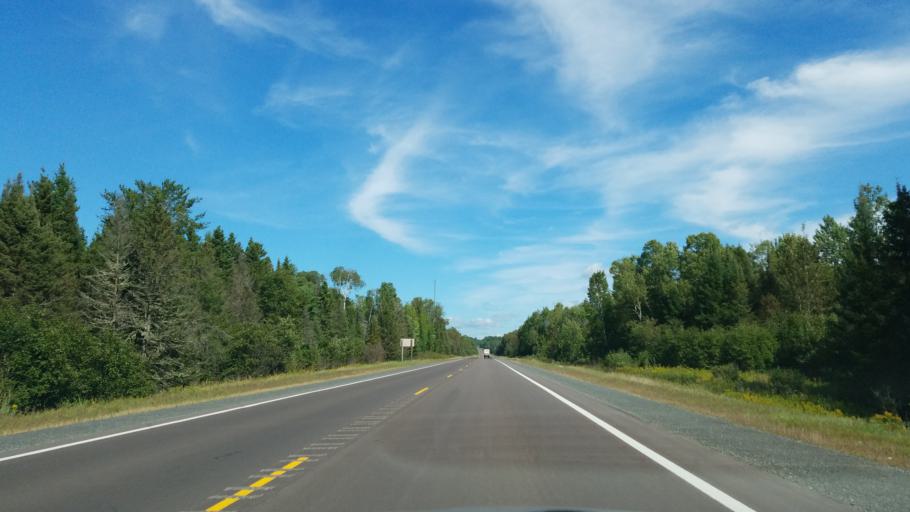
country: US
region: Michigan
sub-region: Baraga County
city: Baraga
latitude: 46.4941
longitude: -88.8253
